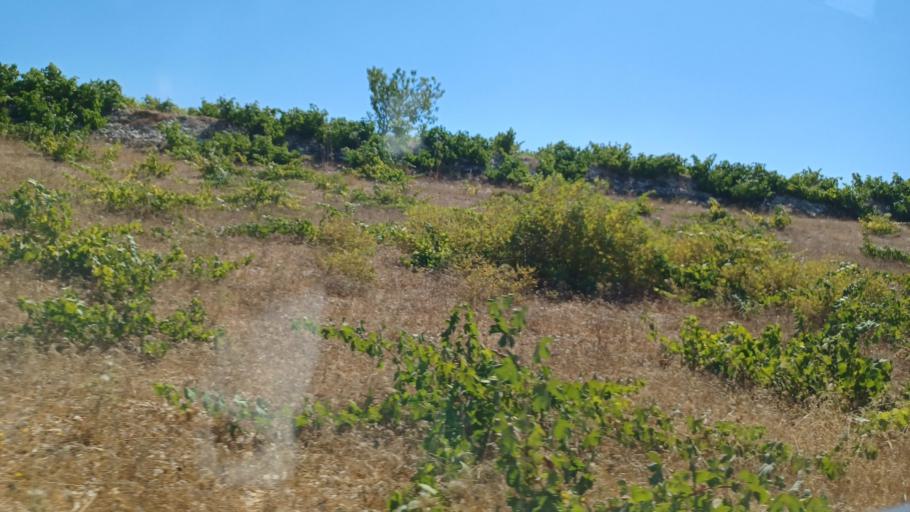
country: CY
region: Pafos
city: Mesogi
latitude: 34.9014
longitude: 32.6313
